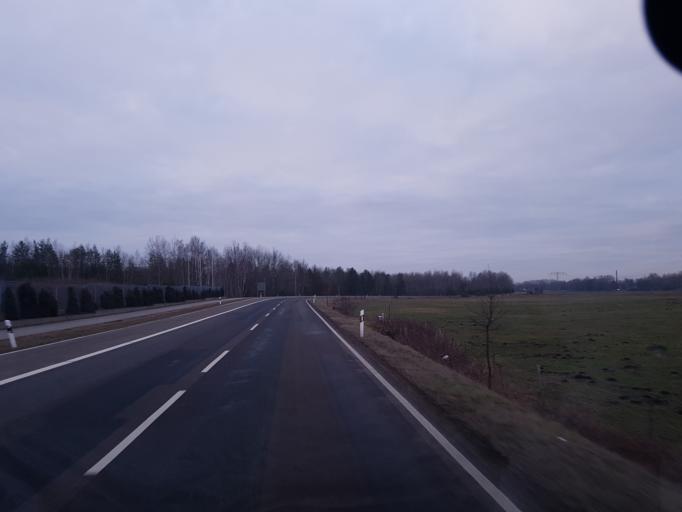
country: DE
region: Brandenburg
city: Schipkau
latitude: 51.5341
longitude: 13.9134
